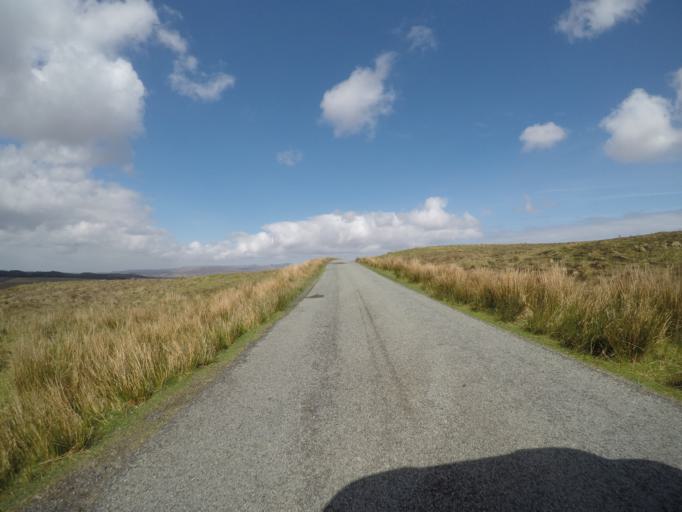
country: GB
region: Scotland
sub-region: Highland
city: Isle of Skye
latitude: 57.4184
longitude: -6.2925
